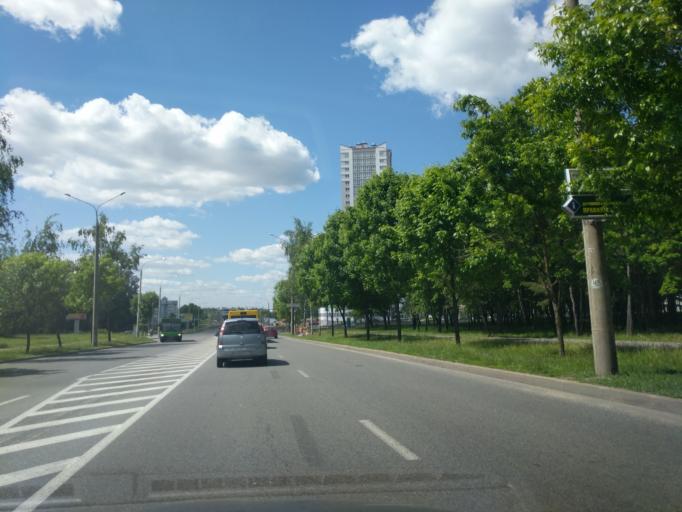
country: BY
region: Minsk
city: Borovlyany
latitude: 53.9268
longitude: 27.6578
